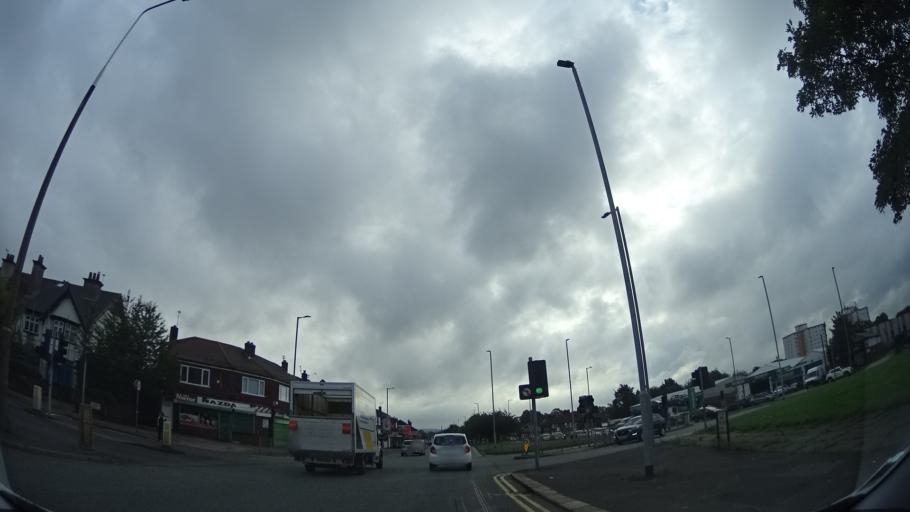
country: GB
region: England
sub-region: Knowsley
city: Knowsley
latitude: 53.4186
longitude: -2.8929
